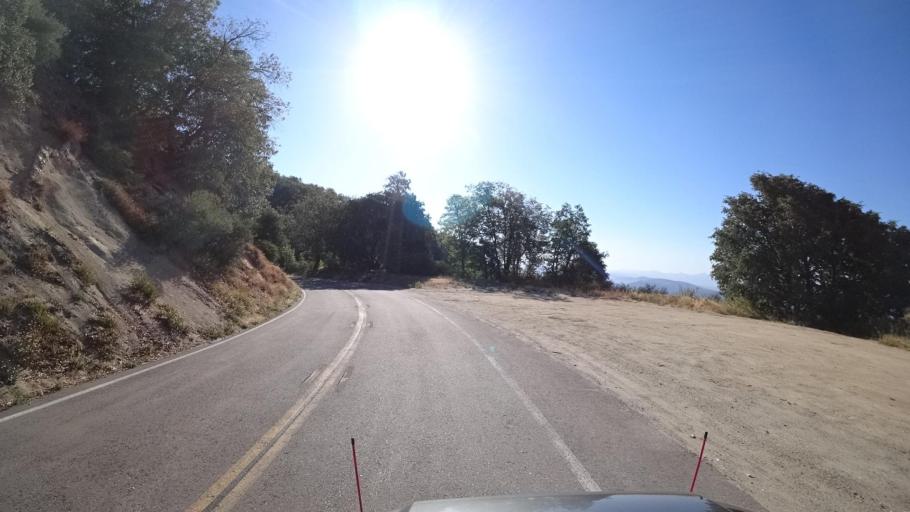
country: US
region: California
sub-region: Riverside County
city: Aguanga
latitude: 33.3034
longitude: -116.8483
